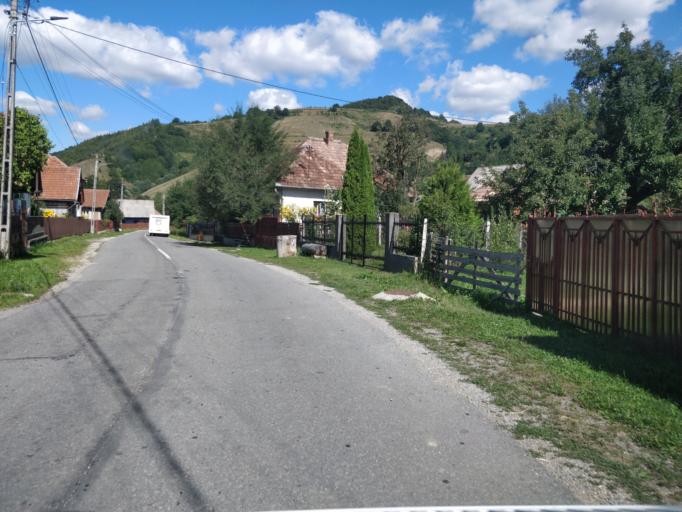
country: RO
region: Cluj
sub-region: Comuna Sacueu
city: Sacuieu
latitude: 46.8257
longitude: 22.8841
